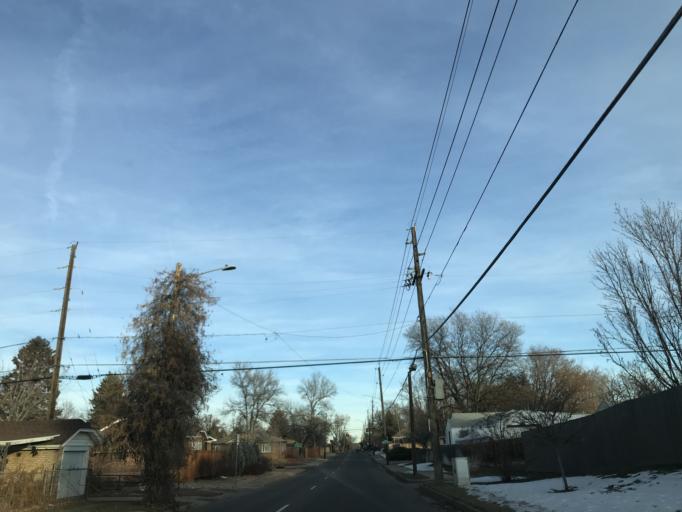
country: US
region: Colorado
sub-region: Arapahoe County
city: Glendale
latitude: 39.7387
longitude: -104.9010
